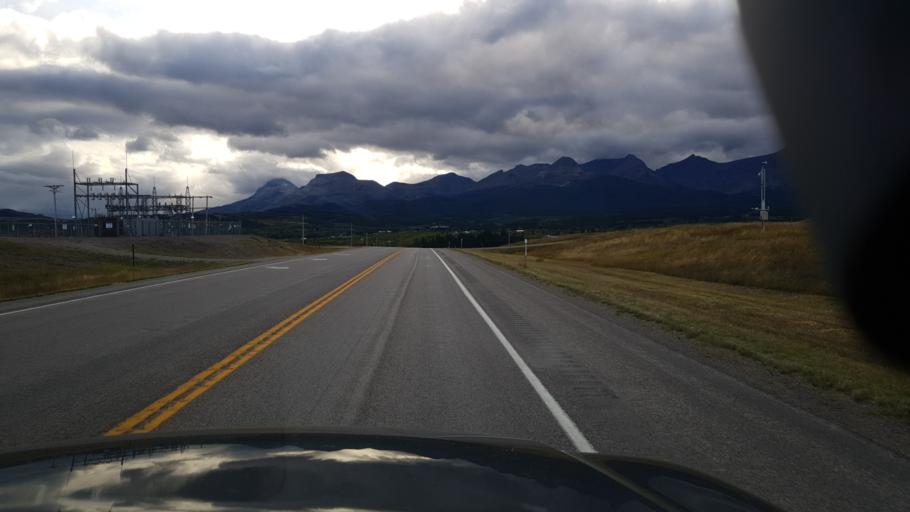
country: US
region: Montana
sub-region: Glacier County
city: South Browning
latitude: 48.4528
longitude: -113.1938
